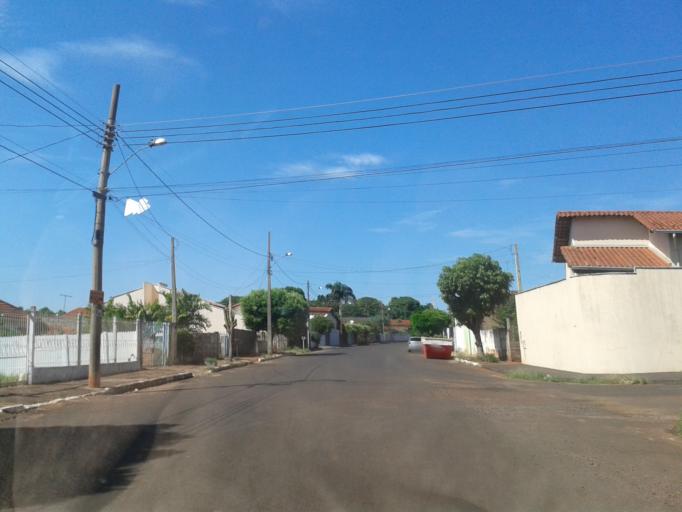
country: BR
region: Minas Gerais
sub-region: Ituiutaba
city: Ituiutaba
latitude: -18.9785
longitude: -49.4733
